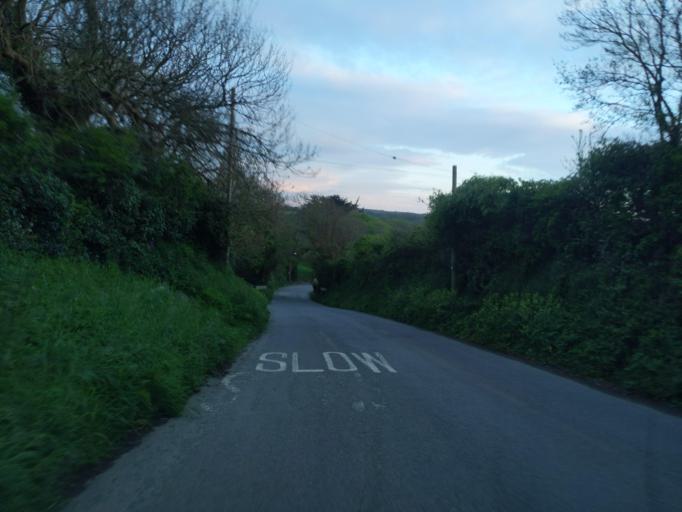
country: GB
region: England
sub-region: Cornwall
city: Polzeath
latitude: 50.5585
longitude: -4.8829
